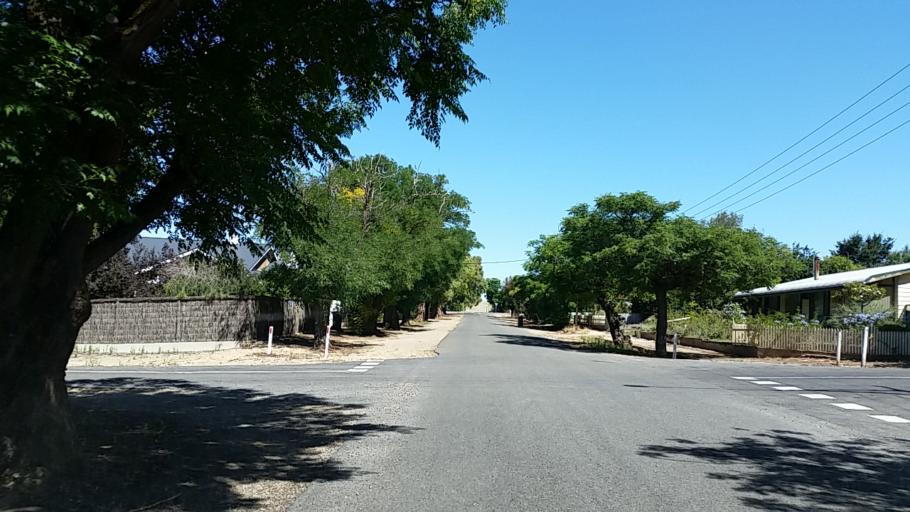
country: AU
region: South Australia
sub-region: Clare and Gilbert Valleys
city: Clare
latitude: -33.6846
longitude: 138.9402
